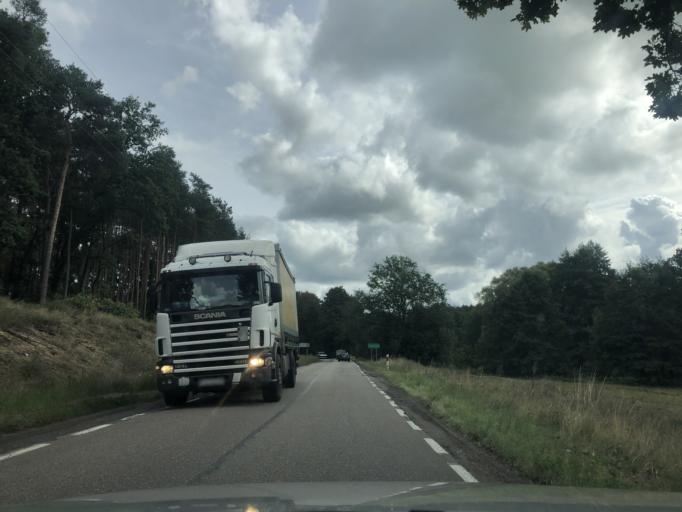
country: PL
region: Greater Poland Voivodeship
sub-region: Powiat czarnkowsko-trzcianecki
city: Wielen
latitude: 52.9028
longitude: 16.1018
